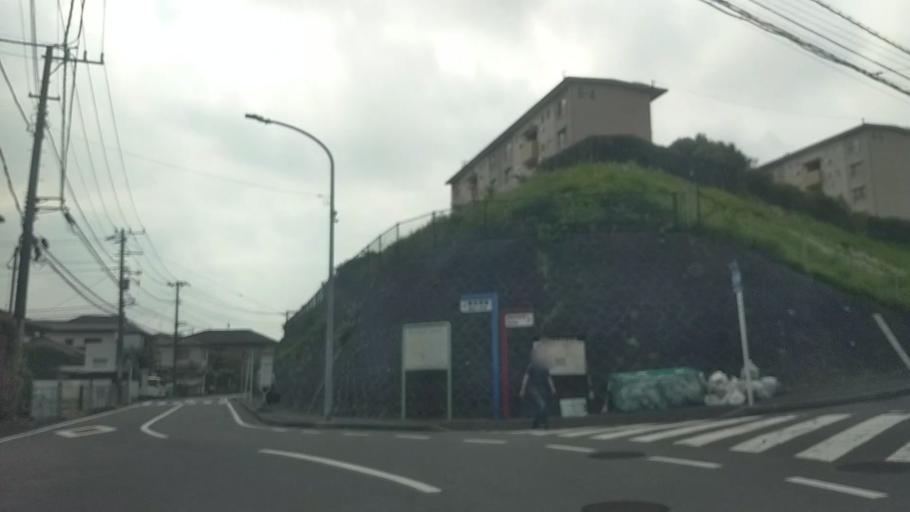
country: JP
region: Kanagawa
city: Kamakura
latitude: 35.3751
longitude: 139.5335
